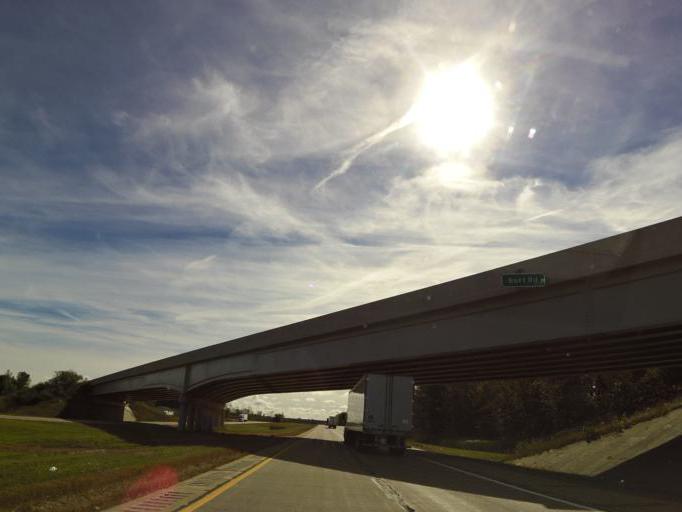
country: US
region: Michigan
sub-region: Saint Clair County
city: Capac
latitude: 42.9846
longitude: -82.8531
